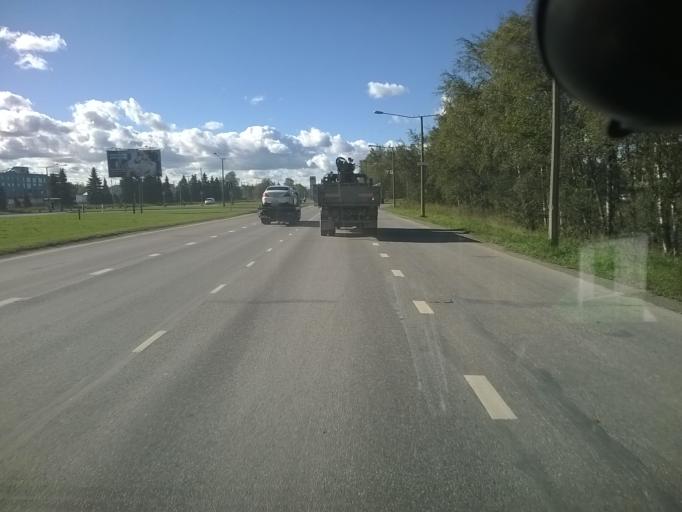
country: EE
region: Harju
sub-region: Tallinna linn
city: Kose
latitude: 59.4341
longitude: 24.8622
